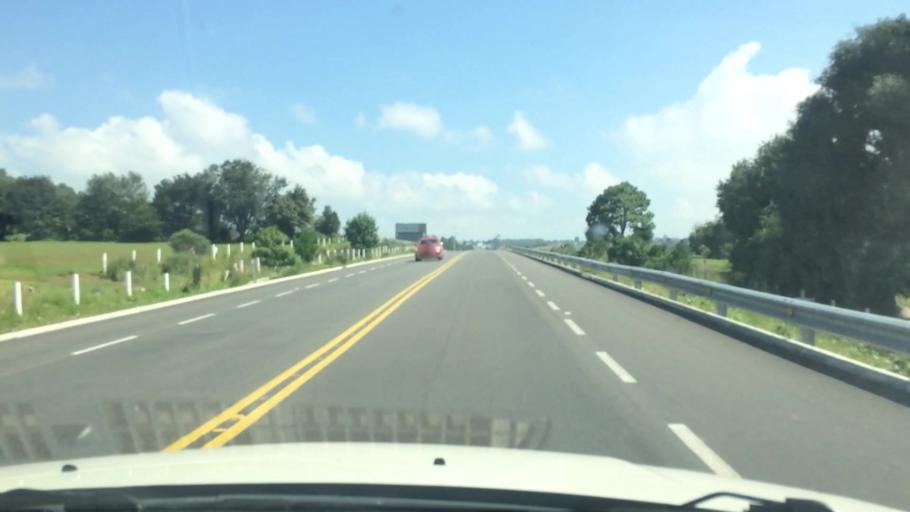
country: MX
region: Mexico
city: Amanalco de Becerra
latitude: 19.3124
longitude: -100.0055
